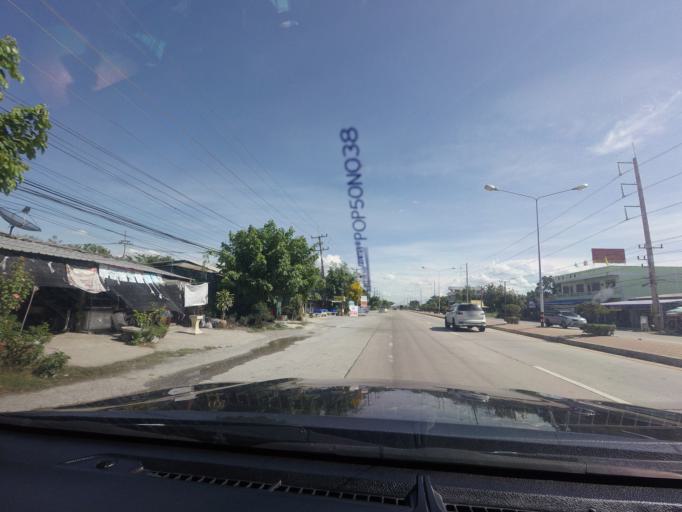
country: TH
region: Suphan Buri
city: Song Phi Nong
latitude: 14.1539
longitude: 99.9842
